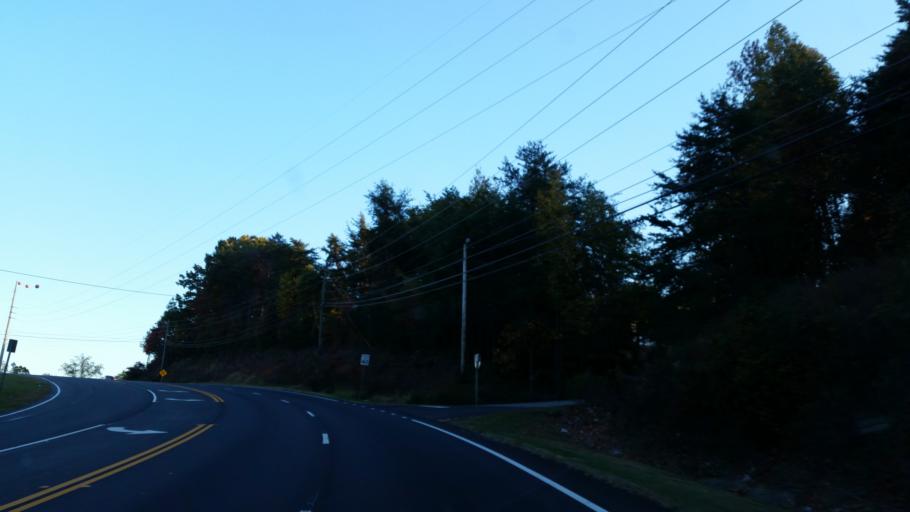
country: US
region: Georgia
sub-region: Lumpkin County
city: Dahlonega
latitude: 34.5249
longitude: -83.9761
